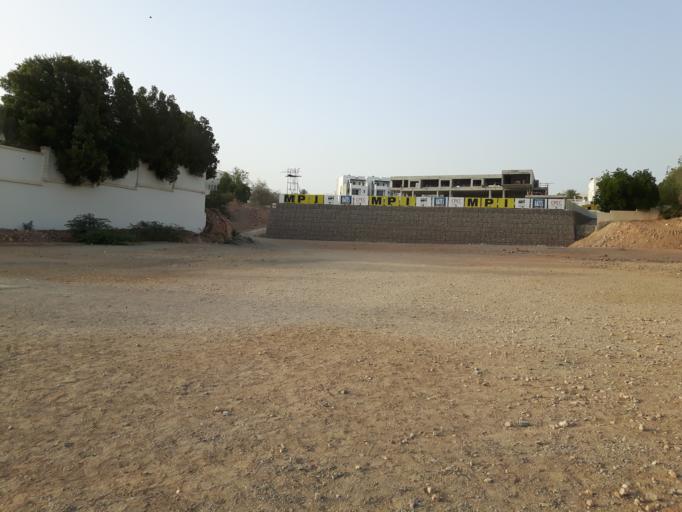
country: OM
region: Muhafazat Masqat
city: Bawshar
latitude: 23.6122
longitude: 58.4719
